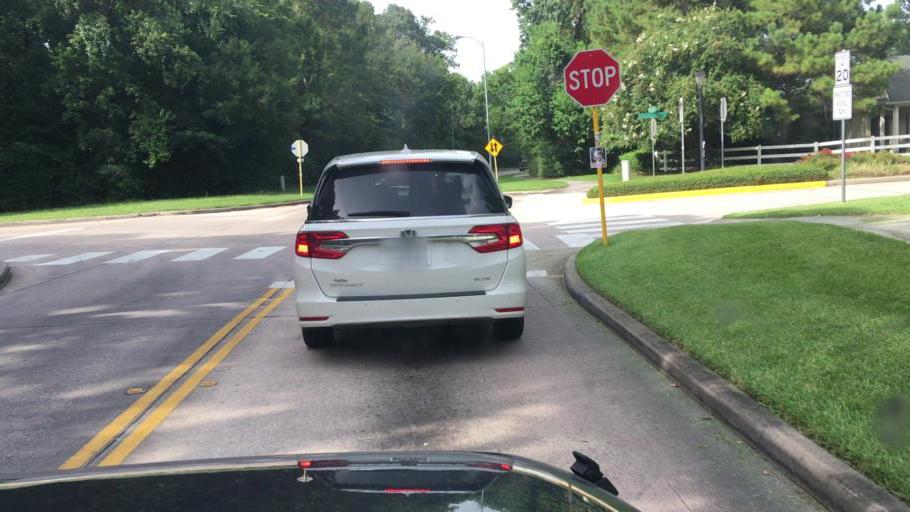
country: US
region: Texas
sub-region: Harris County
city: Atascocita
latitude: 30.0025
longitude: -95.1775
